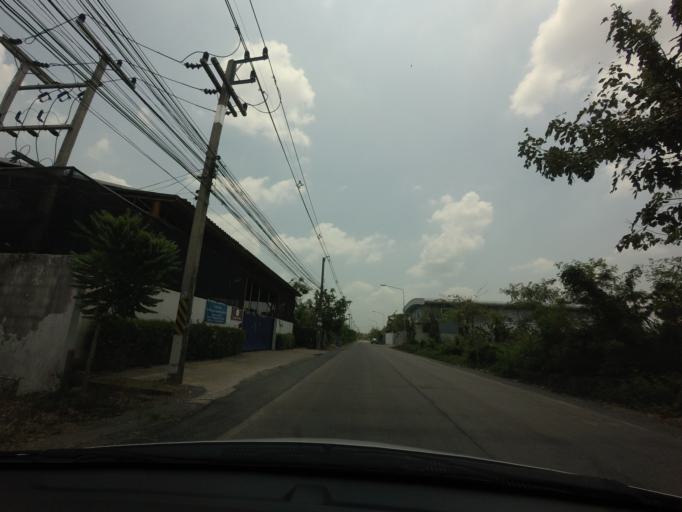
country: TH
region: Pathum Thani
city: Sam Khok
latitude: 14.0441
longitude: 100.5295
